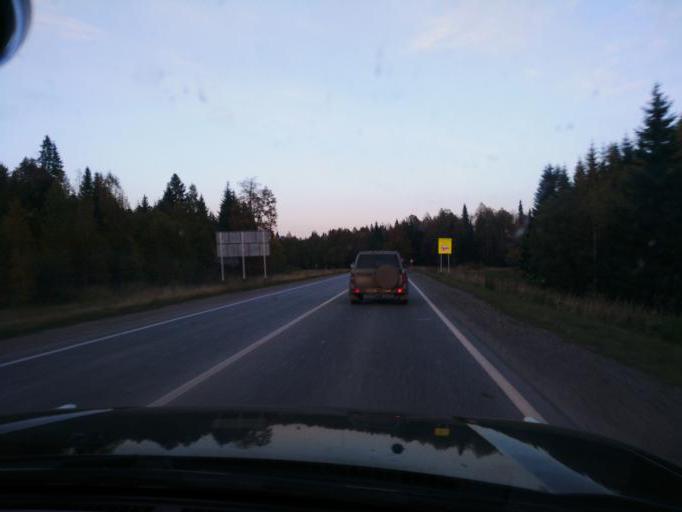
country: RU
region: Perm
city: Polazna
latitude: 58.2996
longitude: 56.6092
